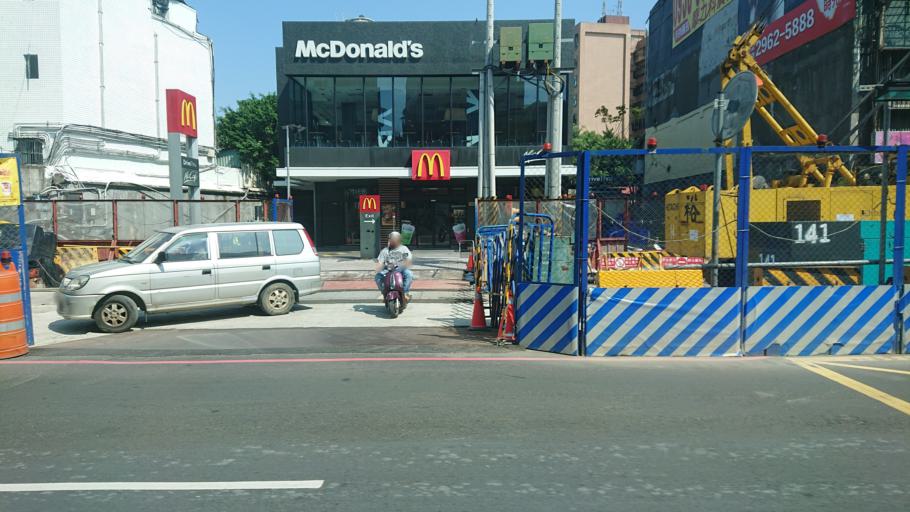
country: TW
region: Taipei
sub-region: Taipei
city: Banqiao
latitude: 25.0268
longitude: 121.5005
